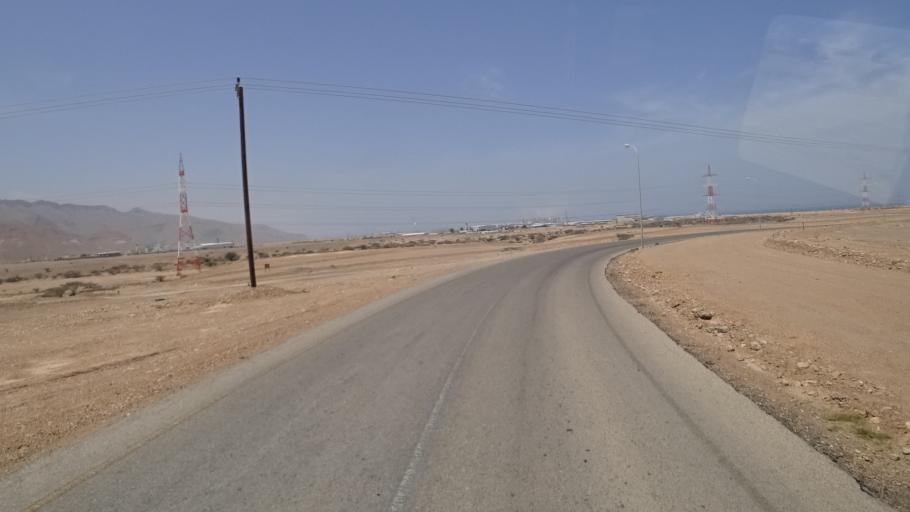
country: OM
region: Ash Sharqiyah
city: Sur
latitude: 22.6073
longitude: 59.4342
